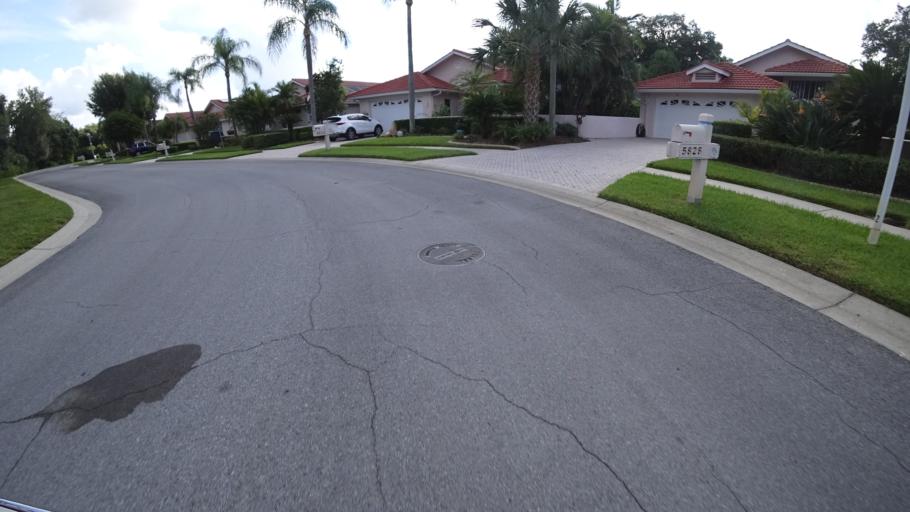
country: US
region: Florida
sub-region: Sarasota County
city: Desoto Lakes
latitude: 27.3958
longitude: -82.4861
